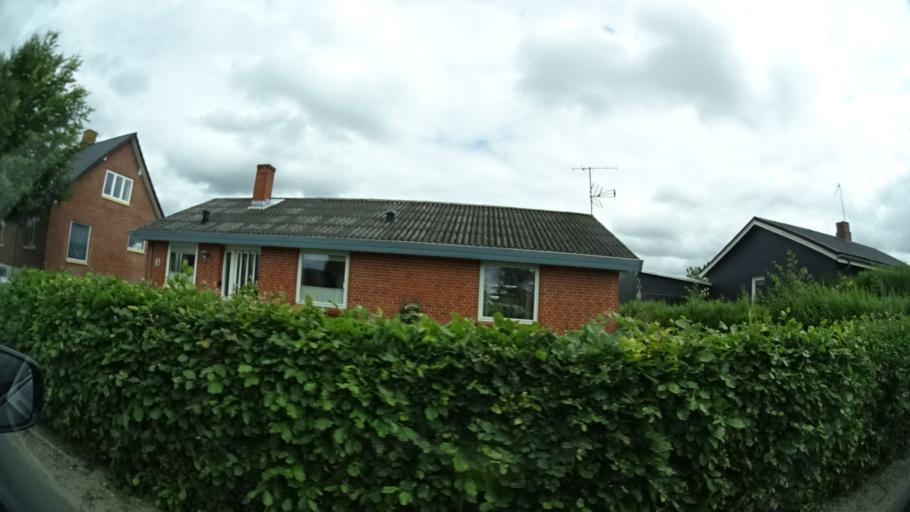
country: DK
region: Central Jutland
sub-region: Norddjurs Kommune
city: Grenaa
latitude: 56.4785
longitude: 10.7246
